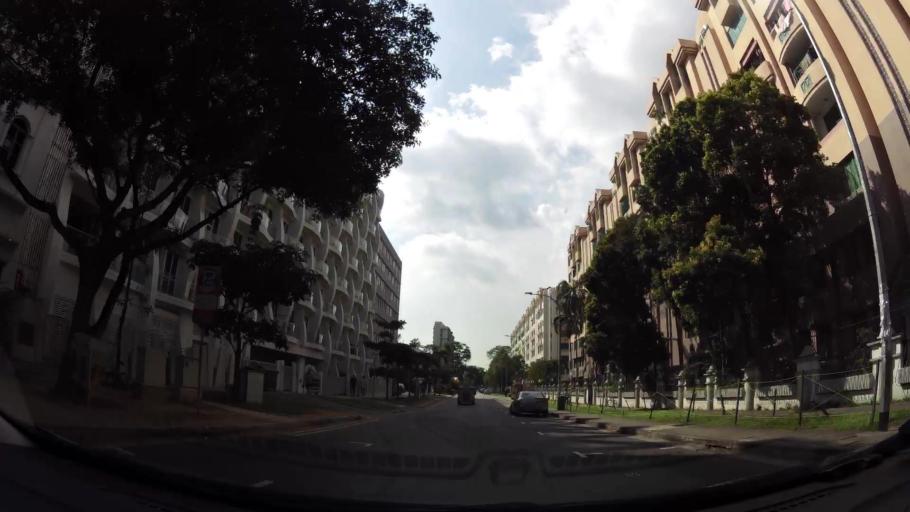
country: SG
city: Singapore
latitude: 1.3122
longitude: 103.8790
